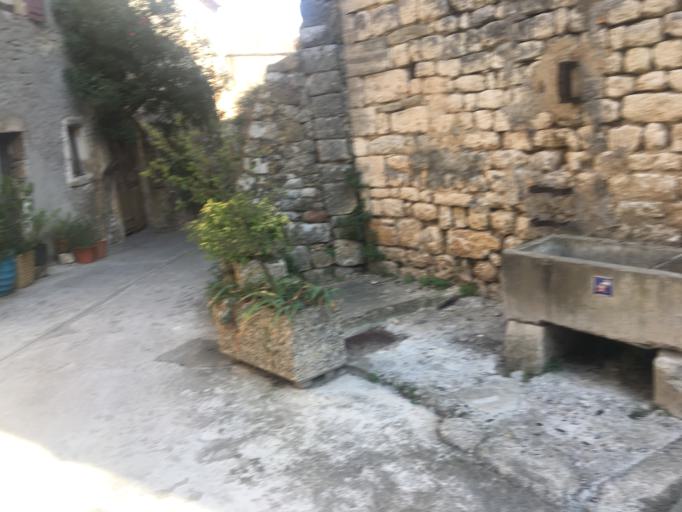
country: FR
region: Languedoc-Roussillon
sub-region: Departement du Gard
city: Saint-Julien-de-Peyrolas
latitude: 44.3044
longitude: 4.5552
